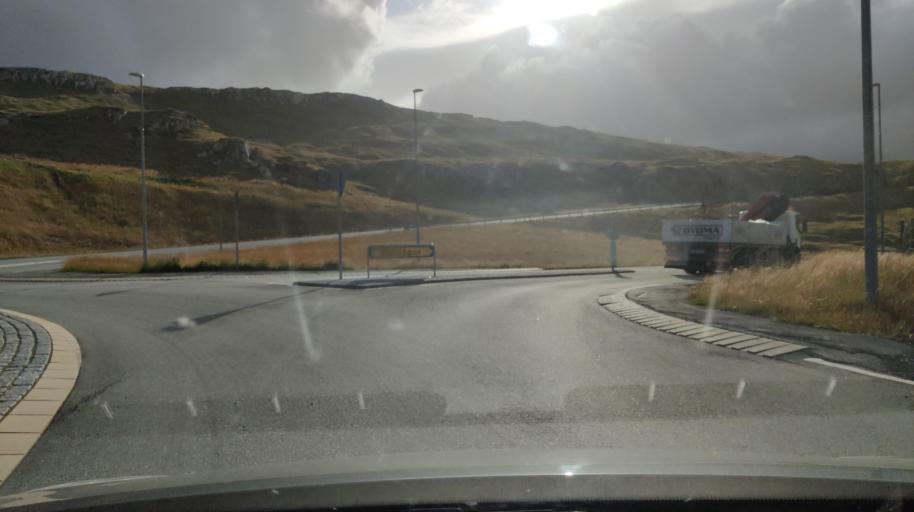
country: FO
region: Streymoy
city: Hoyvik
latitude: 62.0445
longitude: -6.7797
